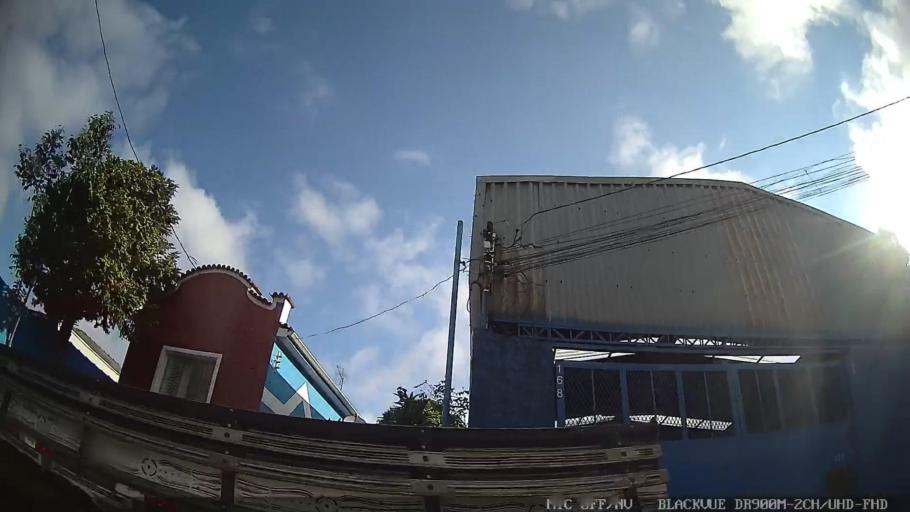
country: BR
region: Sao Paulo
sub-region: Sao Caetano Do Sul
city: Sao Caetano do Sul
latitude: -23.5752
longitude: -46.5323
